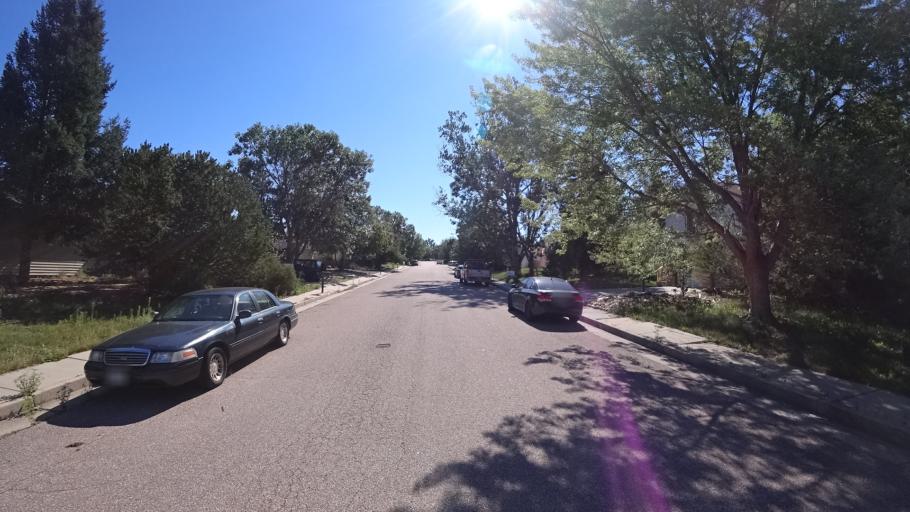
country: US
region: Colorado
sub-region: El Paso County
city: Air Force Academy
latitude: 38.9428
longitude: -104.7918
